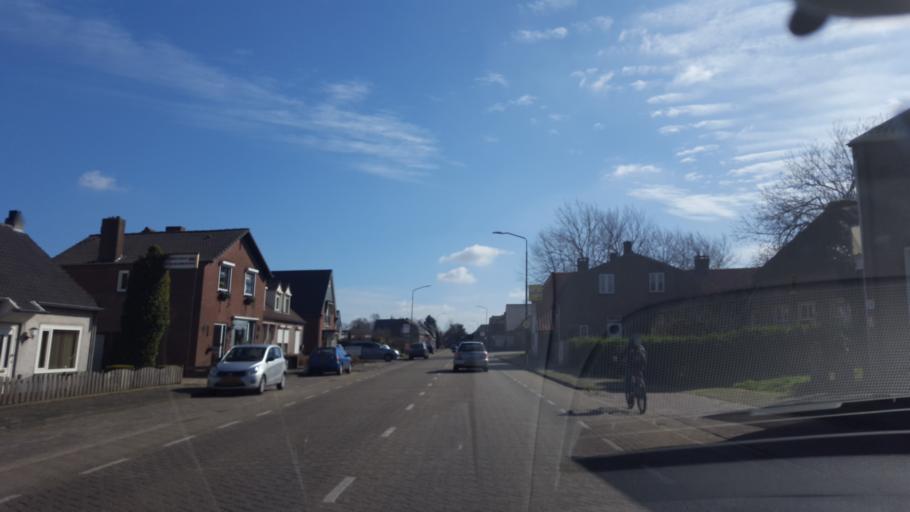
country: NL
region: North Brabant
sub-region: Gemeente Heeze-Leende
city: Heeze
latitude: 51.3740
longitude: 5.5817
